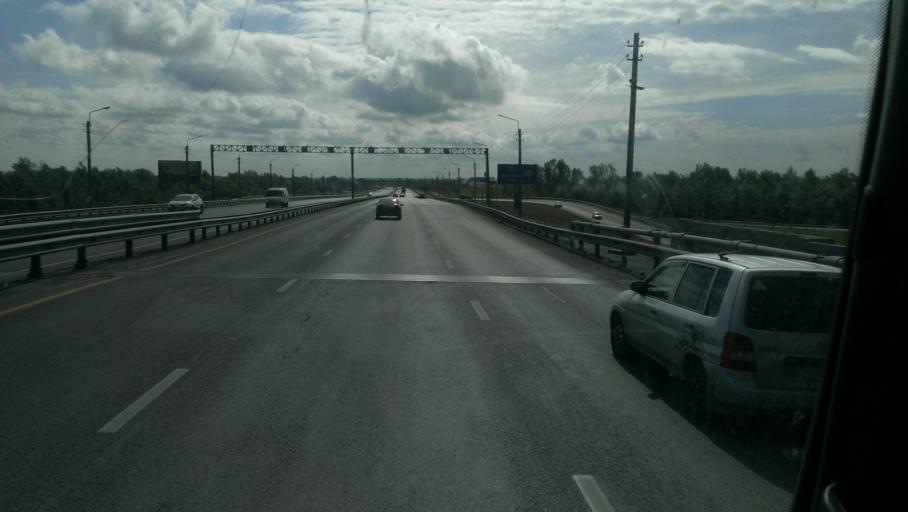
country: RU
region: Altai Krai
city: Zaton
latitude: 53.3208
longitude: 83.8108
